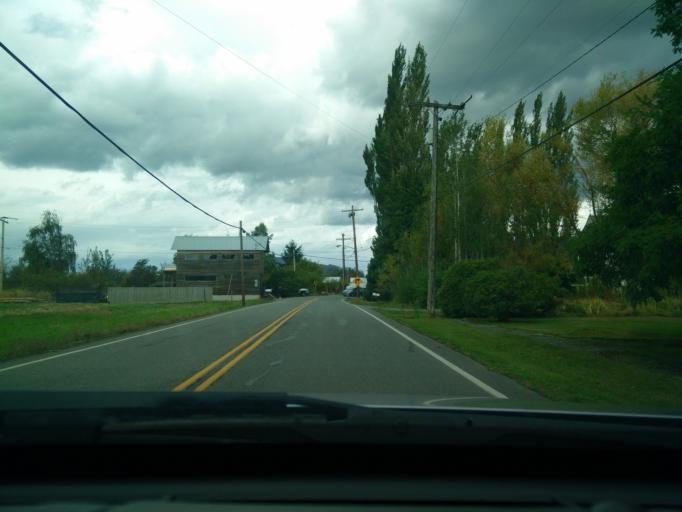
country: US
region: Washington
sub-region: Skagit County
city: Burlington
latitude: 48.5602
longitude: -122.4443
